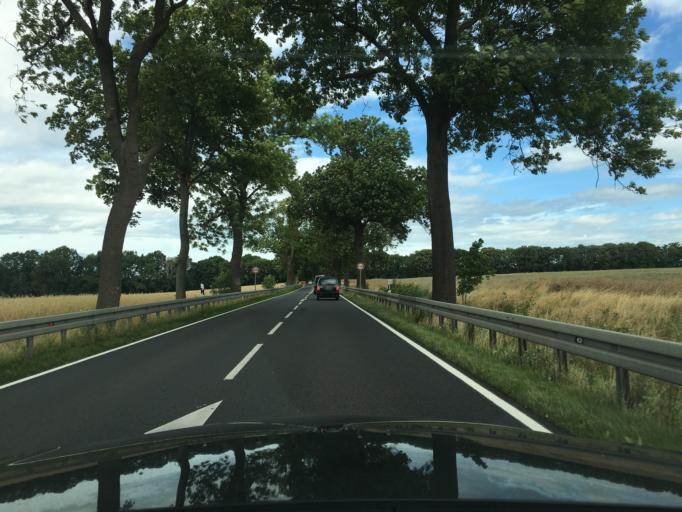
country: DE
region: Brandenburg
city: Gransee
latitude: 52.9584
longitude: 13.1502
